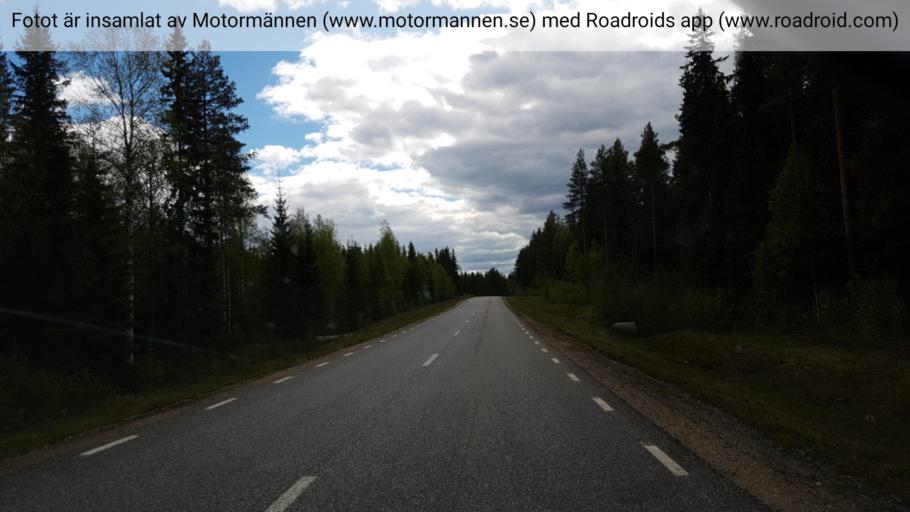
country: SE
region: Vaesterbotten
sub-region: Skelleftea Kommun
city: Langsele
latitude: 64.6379
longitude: 19.9861
